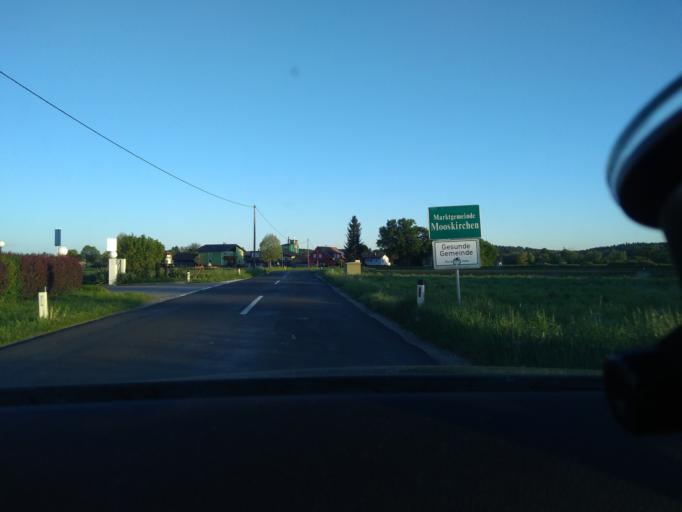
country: AT
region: Styria
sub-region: Politischer Bezirk Voitsberg
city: Mooskirchen
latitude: 46.9920
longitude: 15.2802
